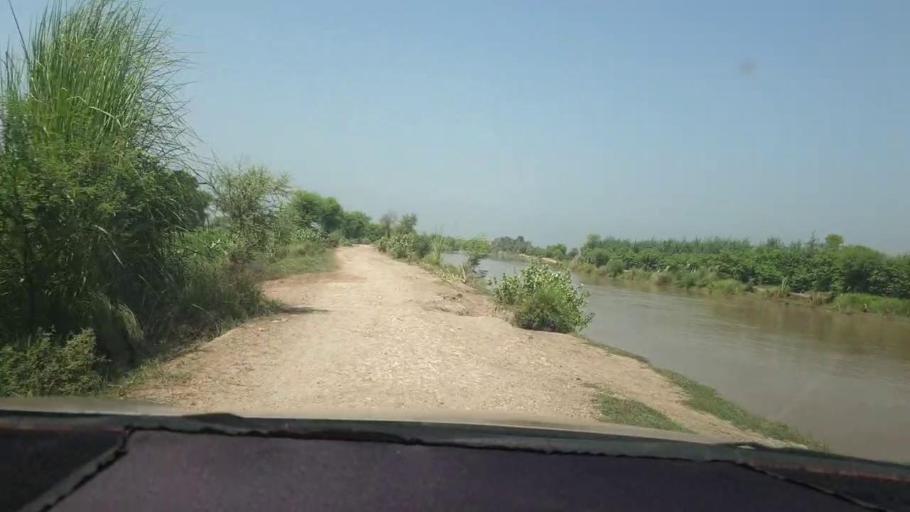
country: PK
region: Sindh
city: Kambar
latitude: 27.6074
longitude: 68.0789
